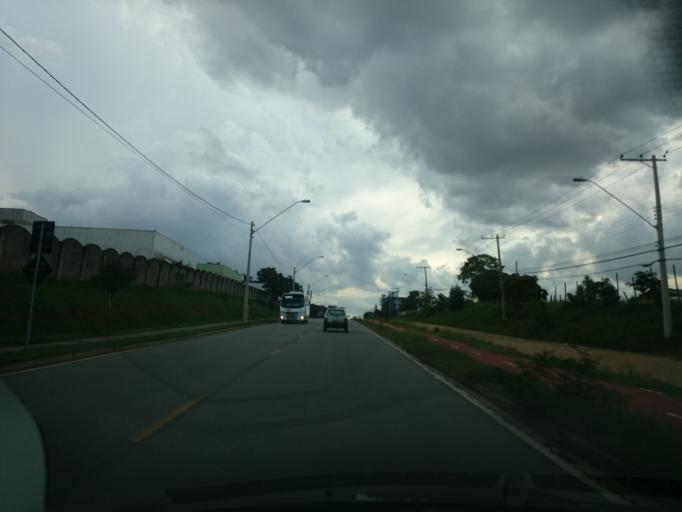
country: BR
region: Sao Paulo
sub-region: Sorocaba
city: Sorocaba
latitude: -23.4776
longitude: -47.4136
